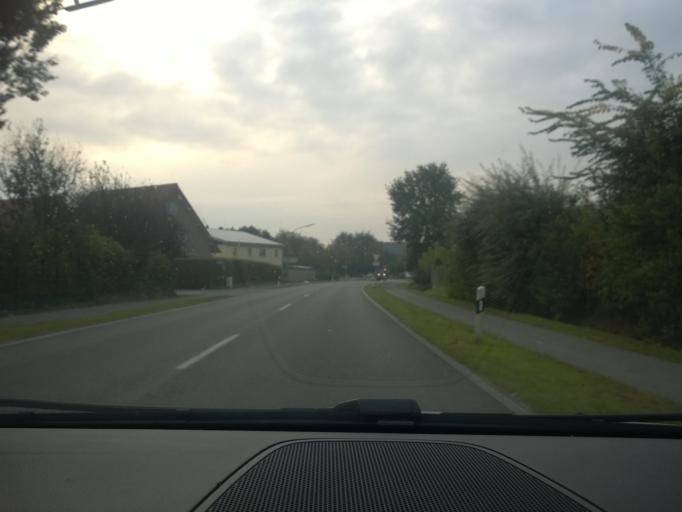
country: DE
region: North Rhine-Westphalia
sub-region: Regierungsbezirk Munster
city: Sudlohn
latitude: 51.9478
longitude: 6.8633
